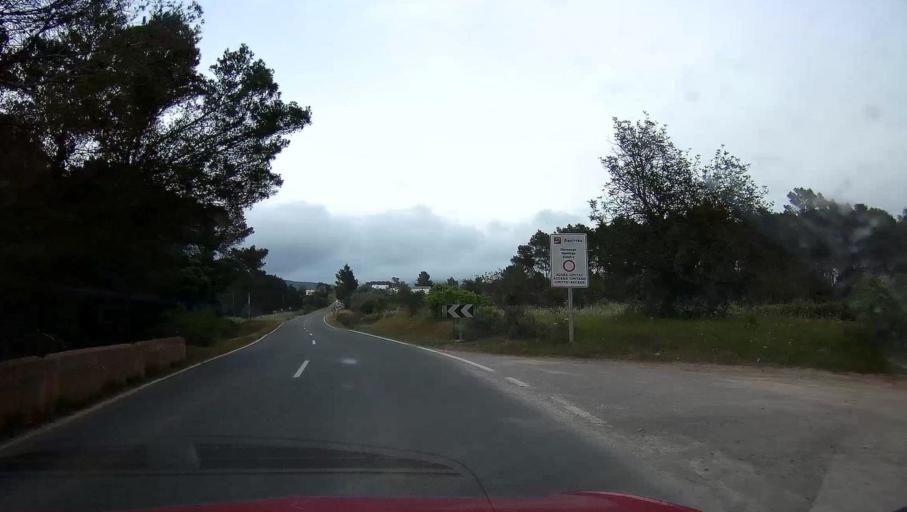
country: ES
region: Balearic Islands
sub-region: Illes Balears
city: Sant Joan de Labritja
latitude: 39.0584
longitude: 1.4641
